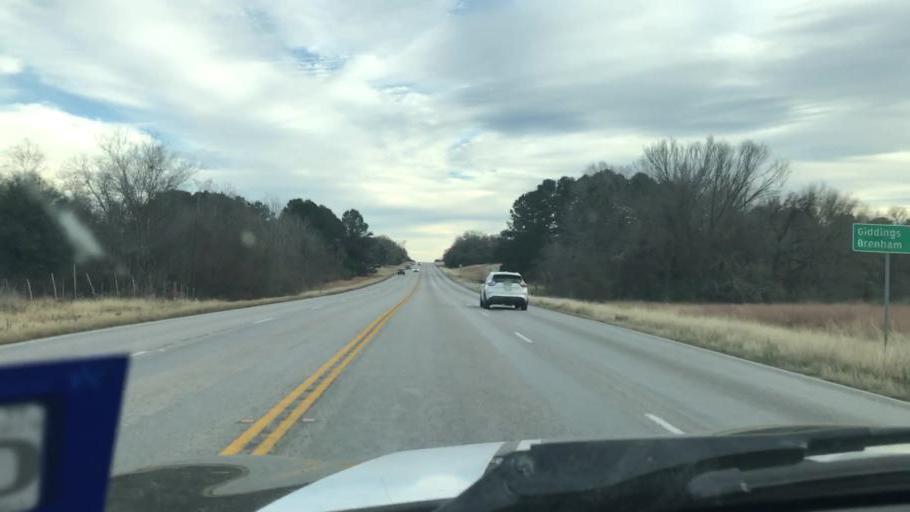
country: US
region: Texas
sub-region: Bastrop County
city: Camp Swift
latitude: 30.2770
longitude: -97.2406
